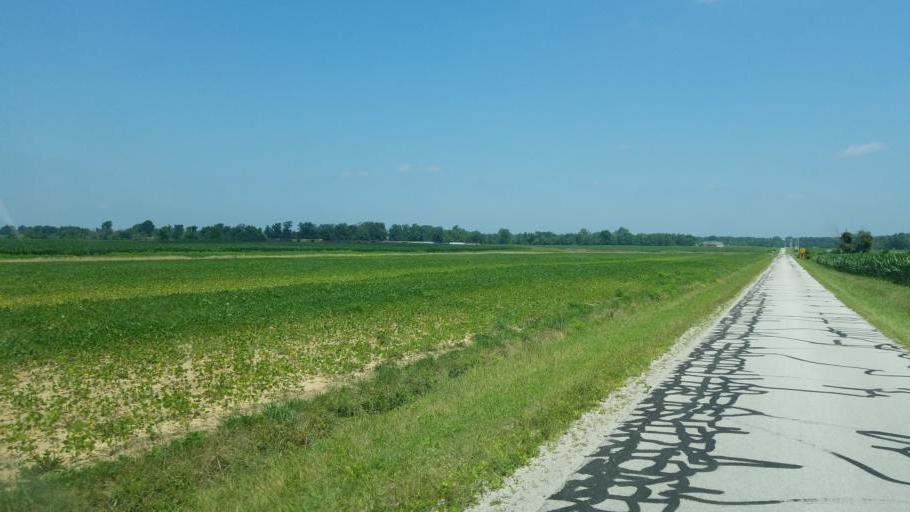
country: US
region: Ohio
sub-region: Sandusky County
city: Green Springs
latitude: 41.1014
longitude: -82.9767
